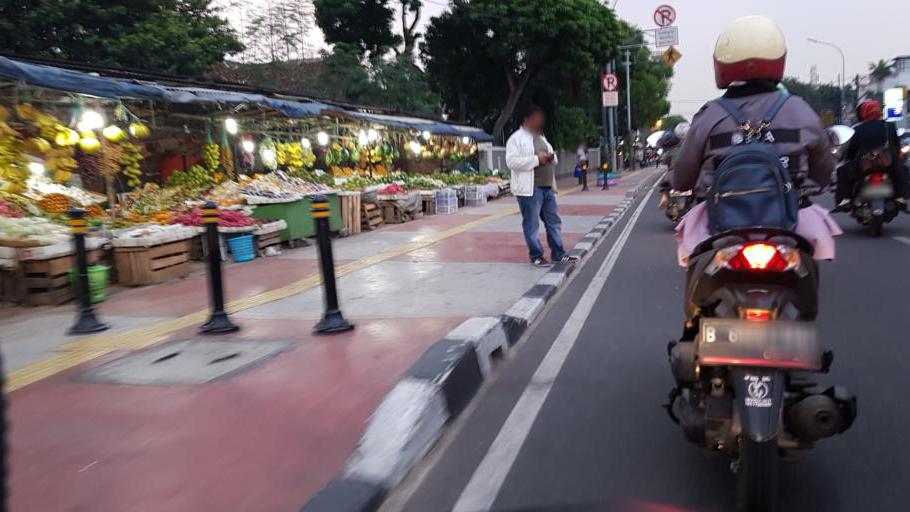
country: ID
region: Jakarta Raya
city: Jakarta
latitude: -6.3052
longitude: 106.8633
